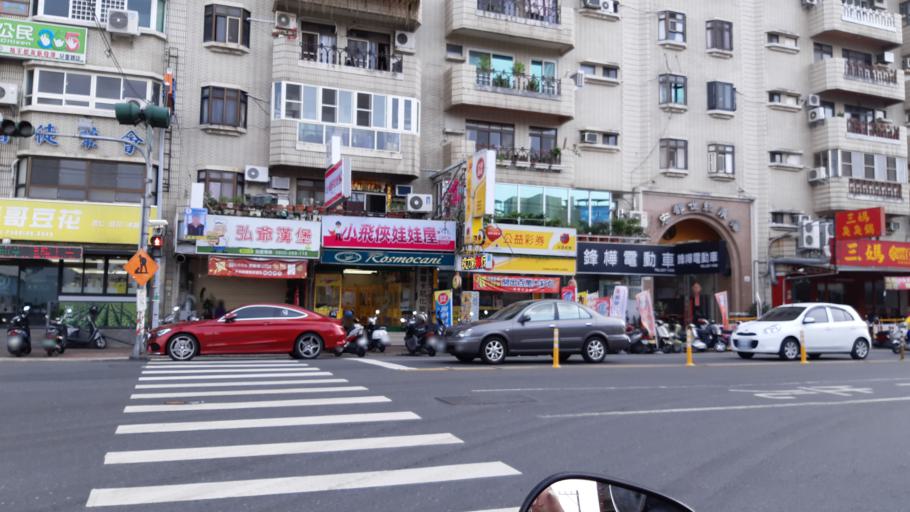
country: TW
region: Taiwan
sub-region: Chiayi
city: Jiayi Shi
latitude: 23.4702
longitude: 120.4611
